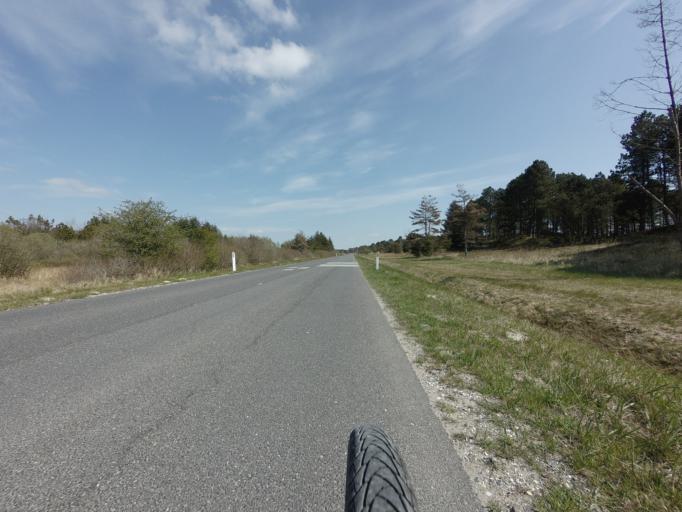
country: DK
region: North Denmark
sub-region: Jammerbugt Kommune
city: Brovst
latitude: 57.2014
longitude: 9.5455
